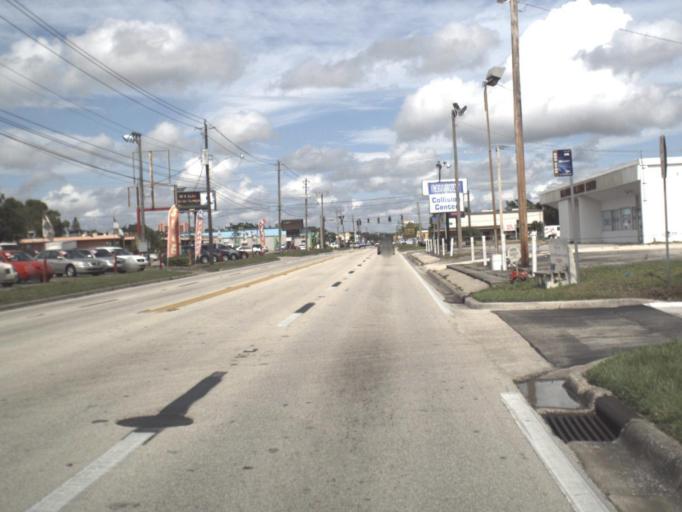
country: US
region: Florida
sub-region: Lee County
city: Fort Myers
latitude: 26.6280
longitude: -81.8620
